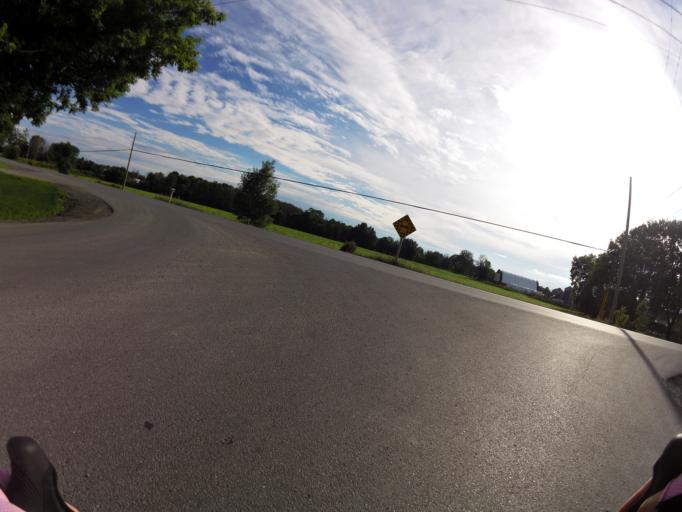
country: CA
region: Ontario
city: Bells Corners
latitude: 45.2522
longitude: -75.7922
